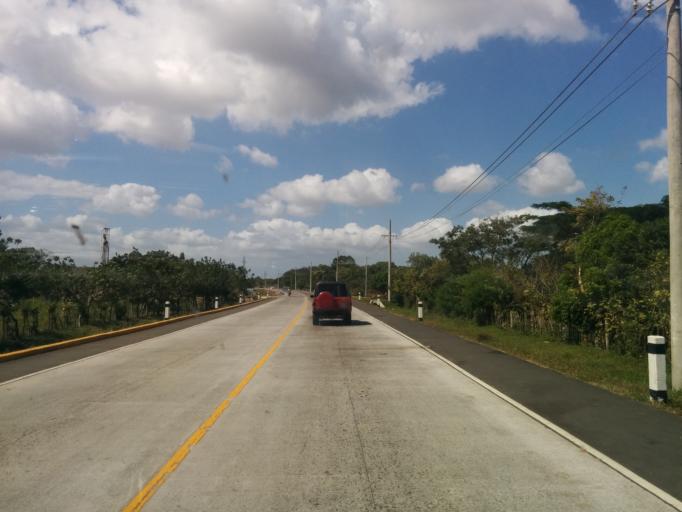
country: NI
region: Masaya
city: Masaya
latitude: 11.9970
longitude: -86.0812
